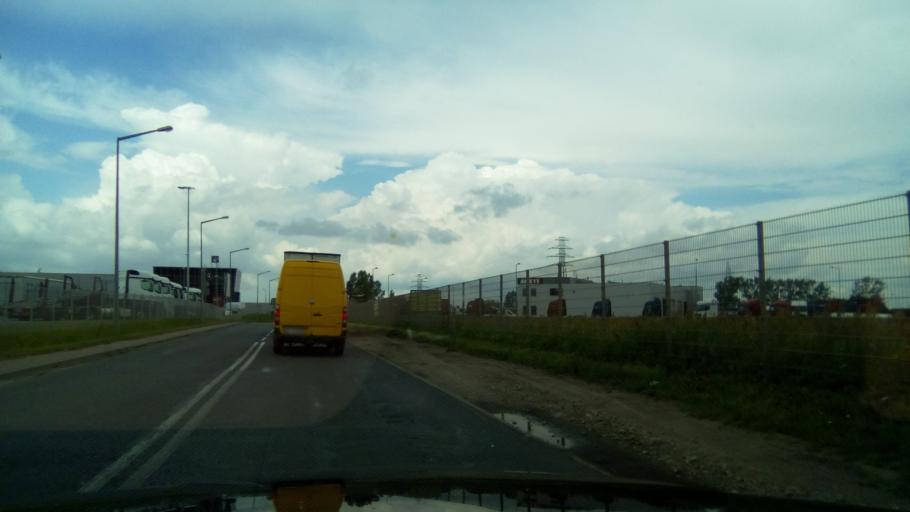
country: PL
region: Greater Poland Voivodeship
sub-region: Powiat poznanski
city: Komorniki
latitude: 52.3476
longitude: 16.8255
